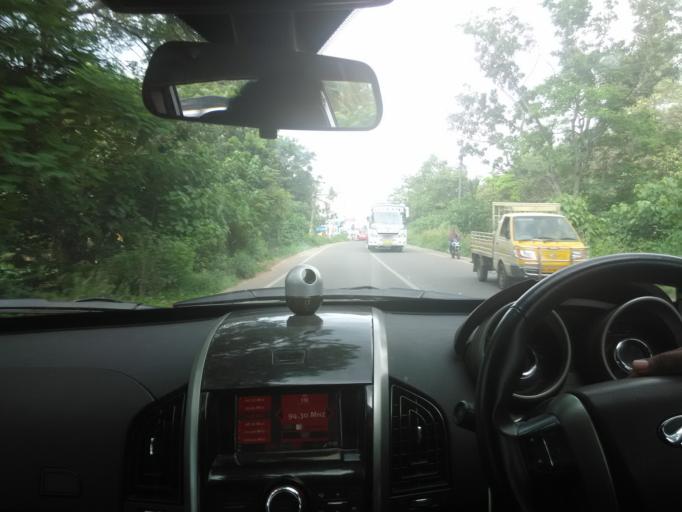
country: IN
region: Kerala
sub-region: Thiruvananthapuram
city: Attingal
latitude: 8.6409
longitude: 76.8442
